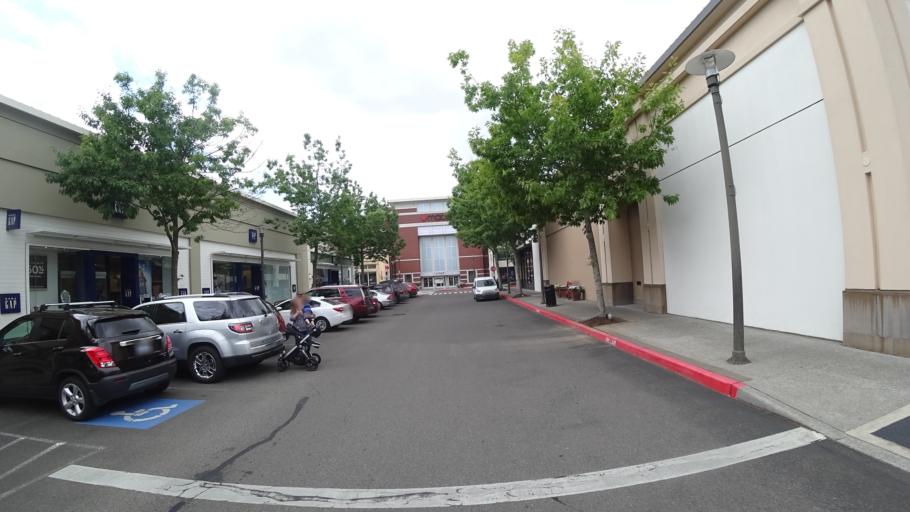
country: US
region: Oregon
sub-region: Washington County
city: Rockcreek
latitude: 45.5357
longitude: -122.8787
